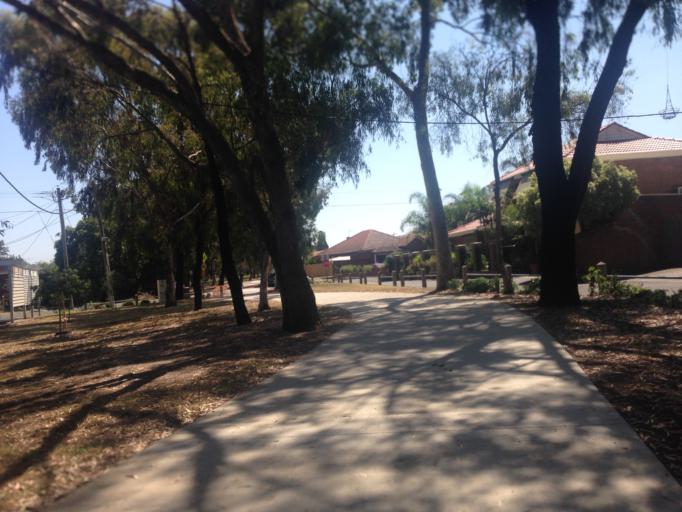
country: AU
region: Victoria
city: Thornbury
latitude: -37.7543
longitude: 144.9891
